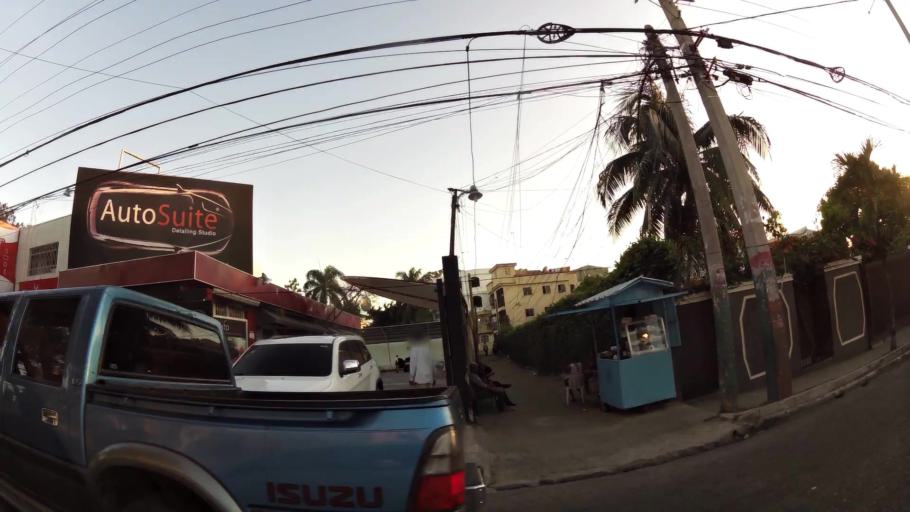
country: DO
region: Nacional
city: La Agustina
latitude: 18.5007
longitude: -69.9598
